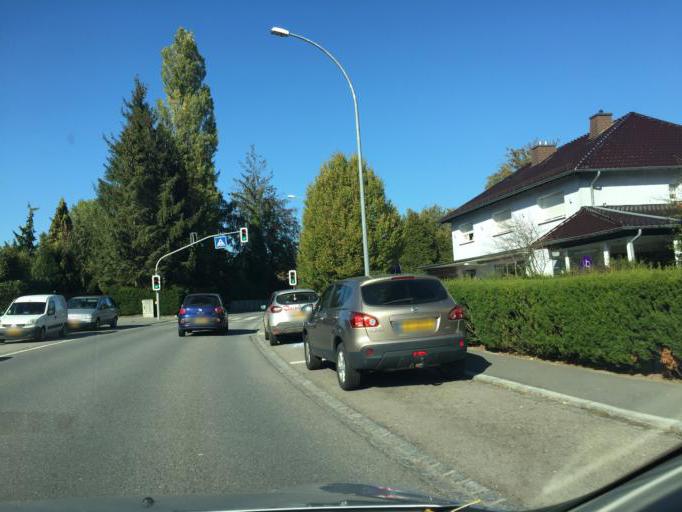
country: LU
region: Luxembourg
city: Bridel
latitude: 49.6509
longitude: 6.0828
